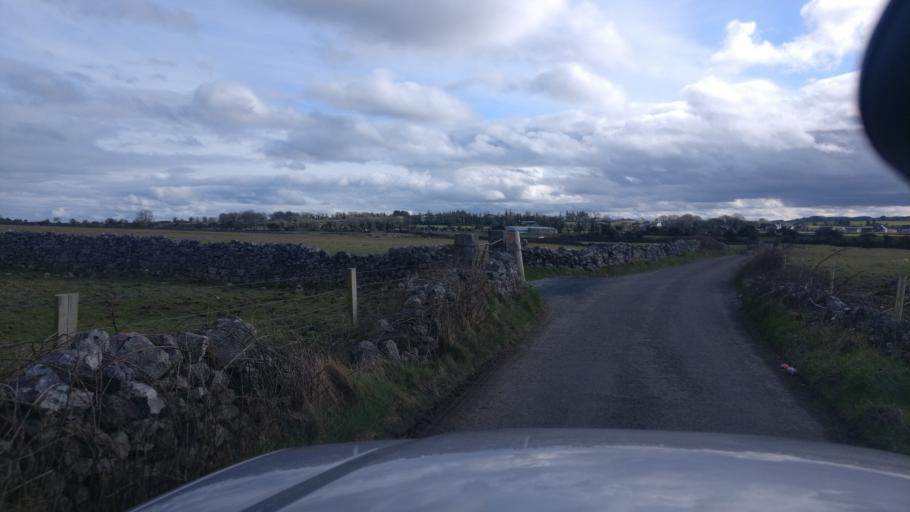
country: IE
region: Connaught
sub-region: County Galway
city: Loughrea
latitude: 53.1996
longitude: -8.5425
